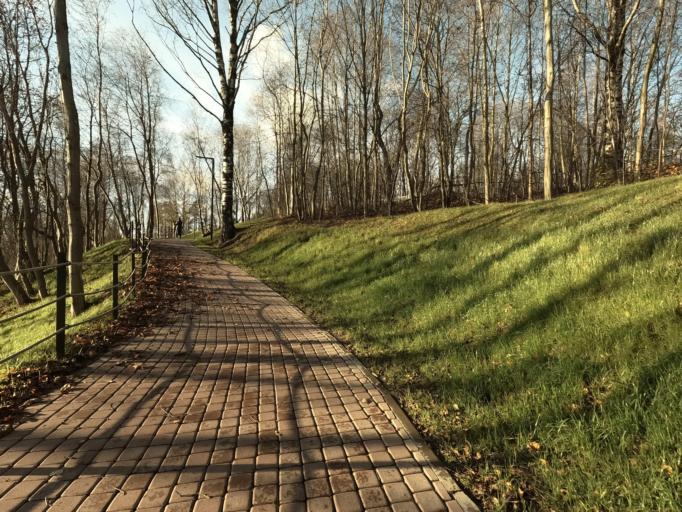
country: RU
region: Leningrad
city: Vsevolozhsk
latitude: 60.0333
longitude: 30.6454
